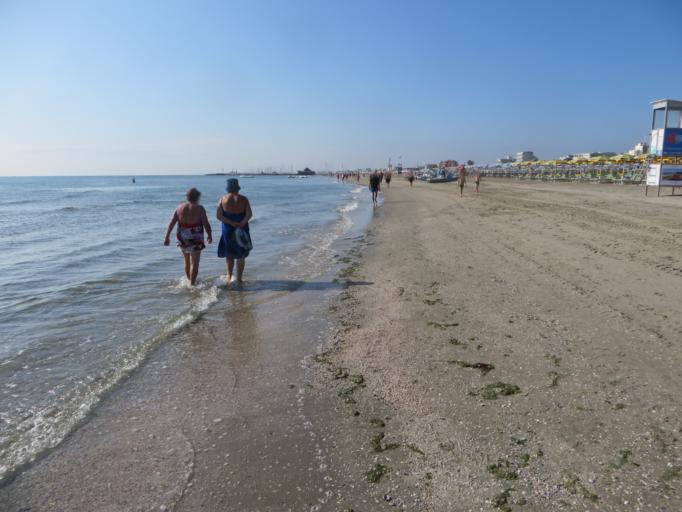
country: IT
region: Emilia-Romagna
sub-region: Provincia di Ravenna
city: Cervia
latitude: 44.2744
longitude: 12.3559
